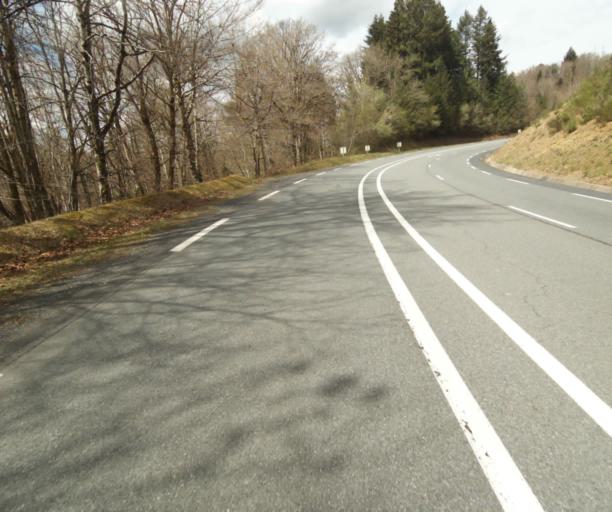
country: FR
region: Limousin
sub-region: Departement de la Correze
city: Sainte-Fortunade
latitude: 45.1926
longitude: 1.8404
